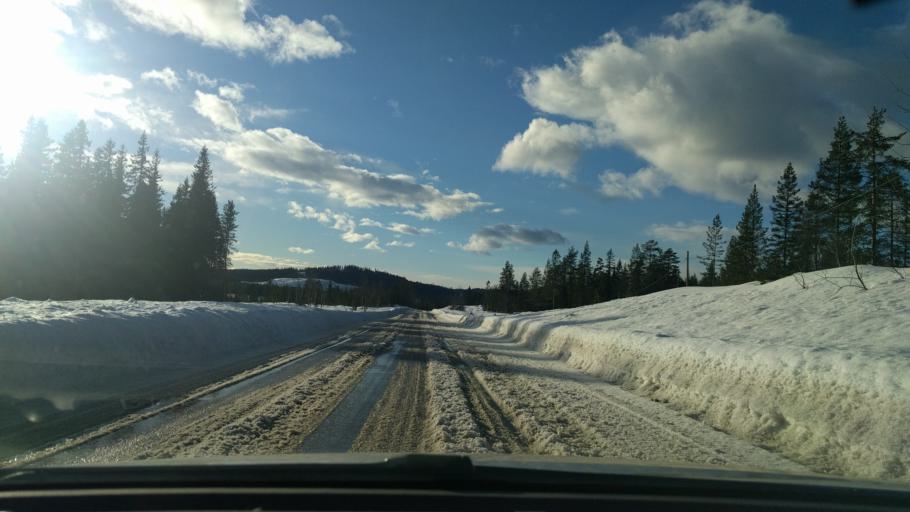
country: NO
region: Hedmark
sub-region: Trysil
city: Innbygda
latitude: 61.0832
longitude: 12.2126
